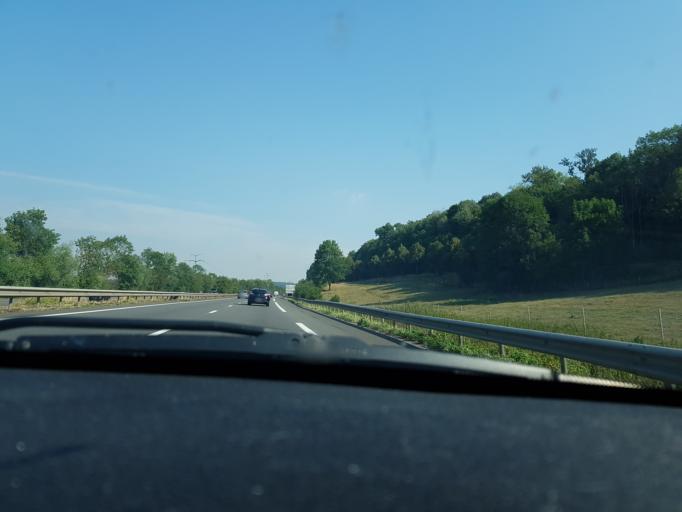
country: FR
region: Lorraine
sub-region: Departement de Meurthe-et-Moselle
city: Frouard
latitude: 48.7656
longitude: 6.1446
